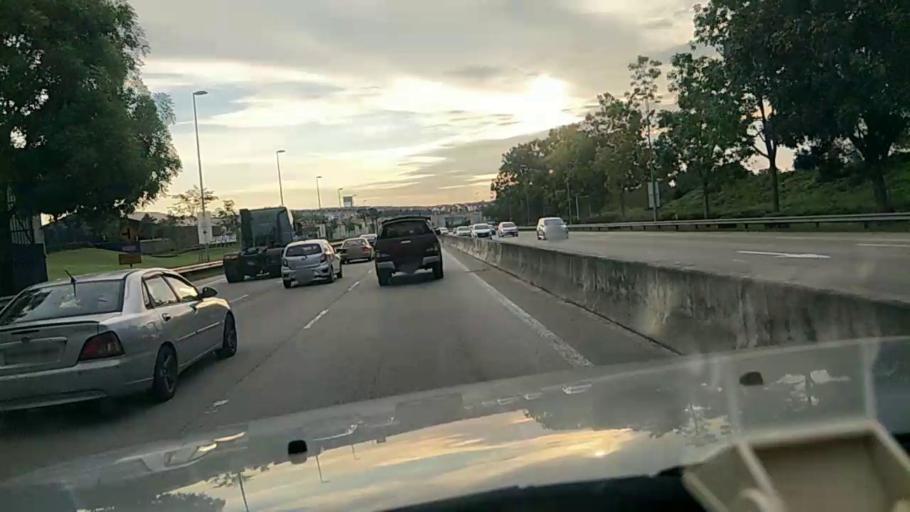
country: MY
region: Selangor
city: Shah Alam
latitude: 3.0995
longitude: 101.4794
